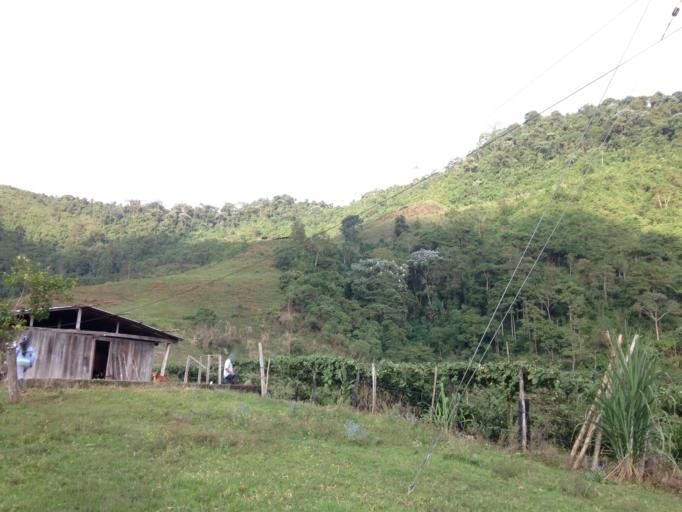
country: CO
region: Valle del Cauca
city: Ginebra
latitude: 3.7686
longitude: -76.1835
